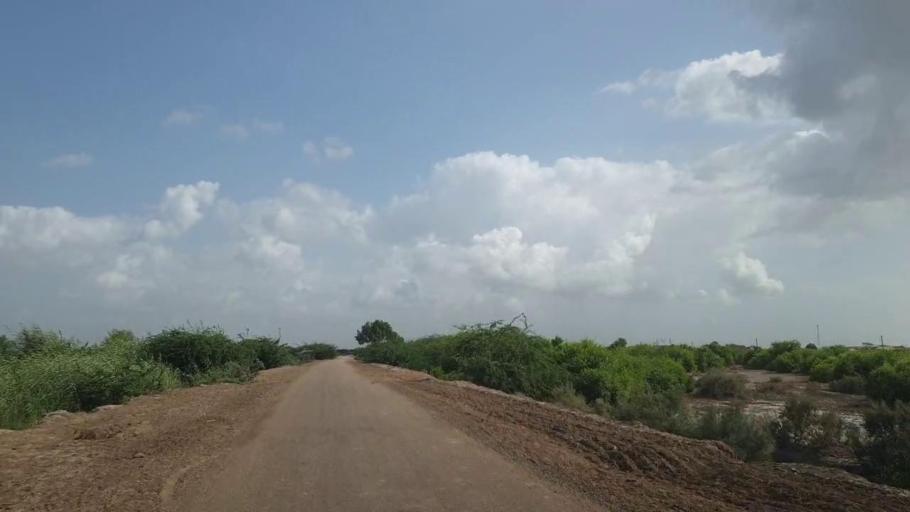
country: PK
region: Sindh
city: Kadhan
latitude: 24.5546
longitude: 69.0637
